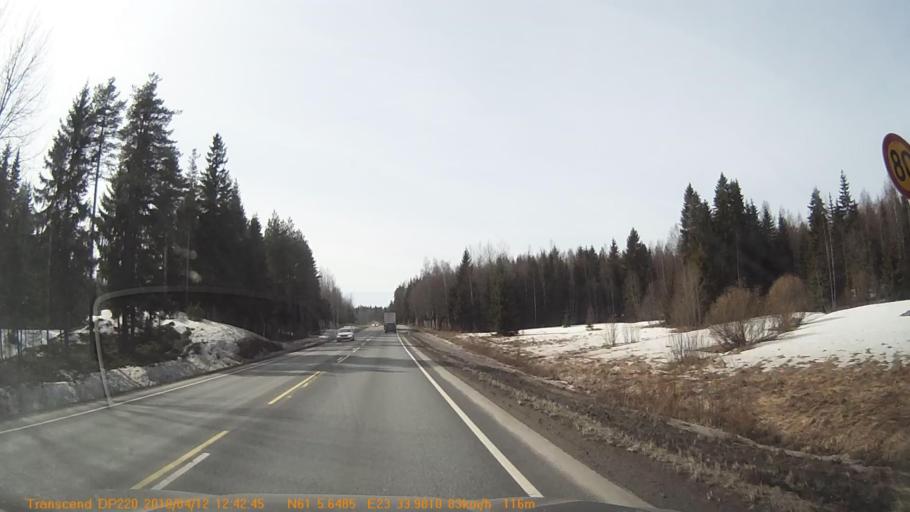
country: FI
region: Pirkanmaa
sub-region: Etelae-Pirkanmaa
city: Urjala
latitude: 61.0940
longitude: 23.5659
